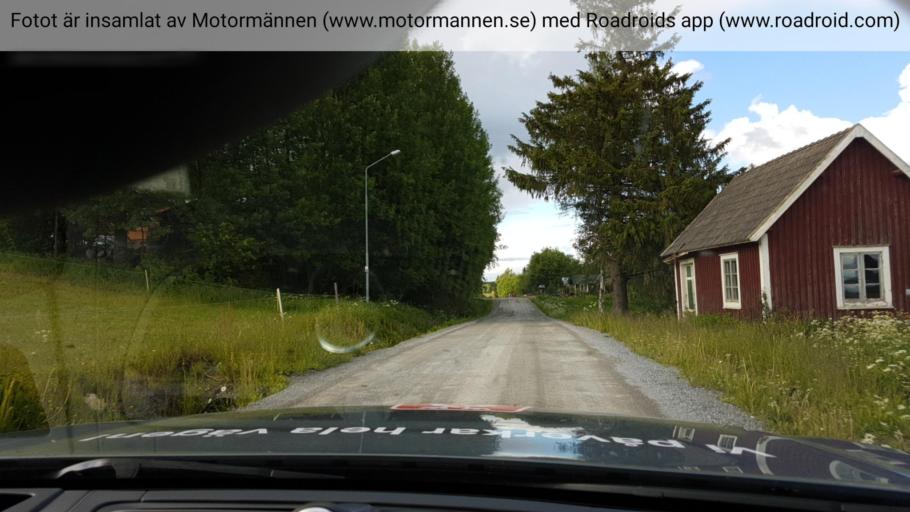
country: SE
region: Jaemtland
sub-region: Bergs Kommun
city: Hoverberg
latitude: 62.9445
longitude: 14.2695
